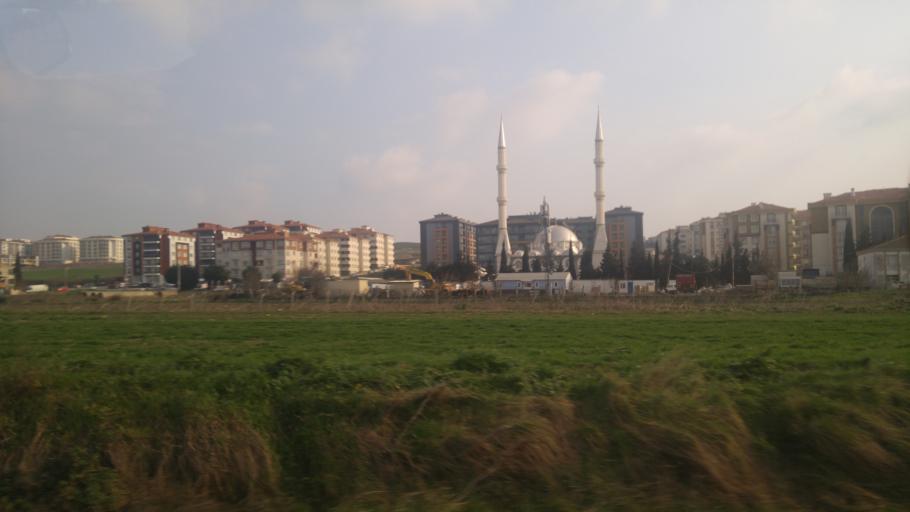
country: TR
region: Istanbul
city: Silivri
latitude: 41.0843
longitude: 28.2638
